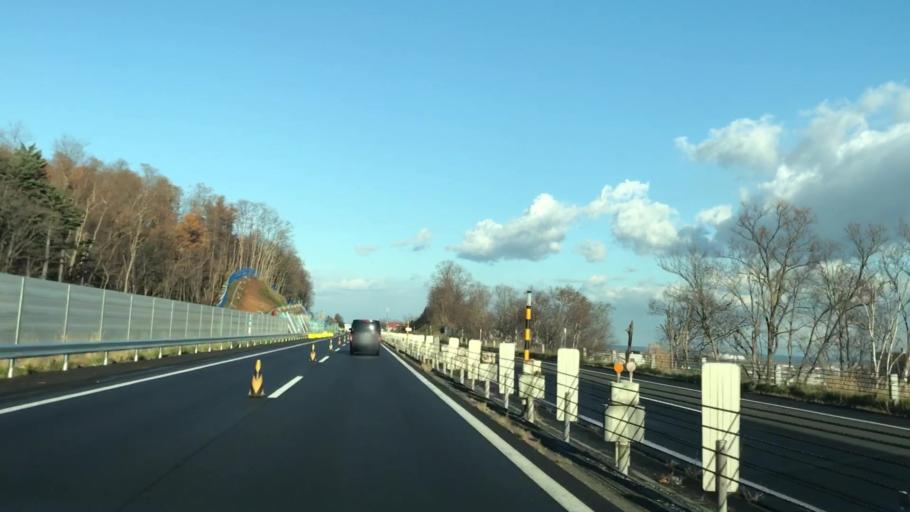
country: JP
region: Hokkaido
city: Sapporo
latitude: 43.1115
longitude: 141.2389
